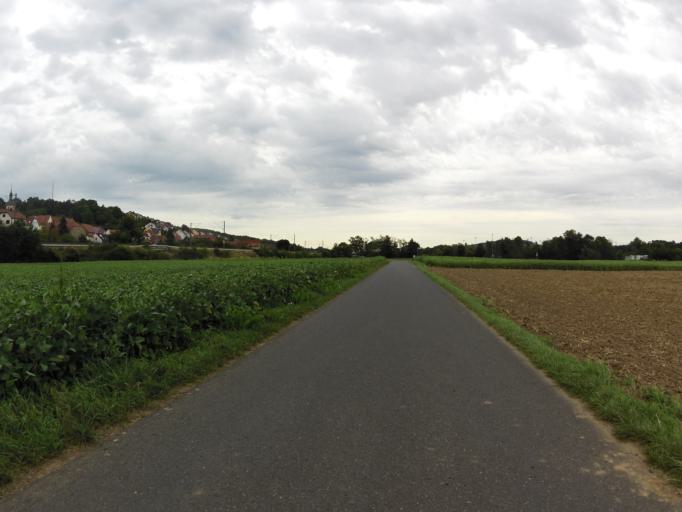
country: DE
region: Bavaria
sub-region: Regierungsbezirk Unterfranken
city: Gadheim
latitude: 50.0218
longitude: 10.3394
